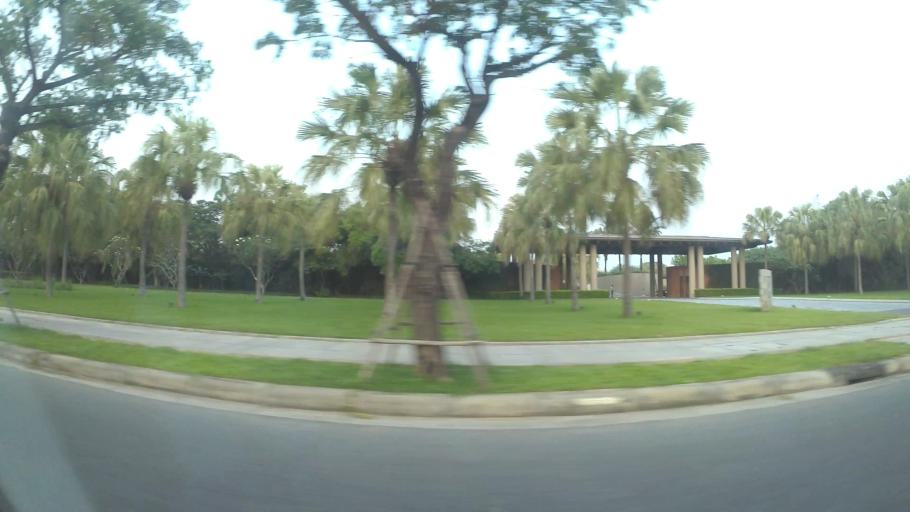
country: VN
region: Da Nang
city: Ngu Hanh Son
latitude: 16.0124
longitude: 108.2624
